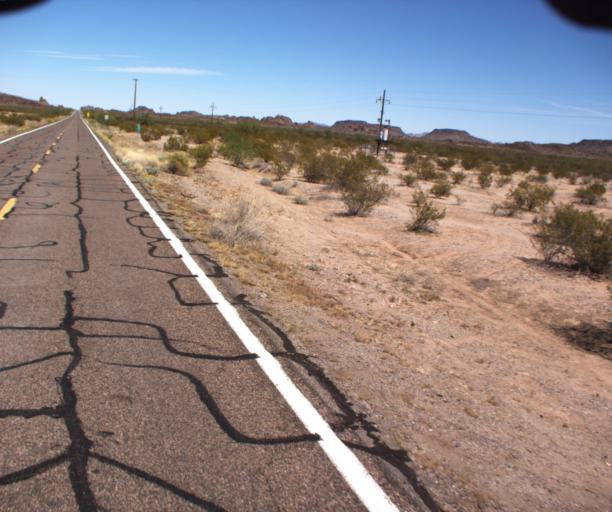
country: US
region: Arizona
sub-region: Pima County
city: Ajo
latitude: 32.5270
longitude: -112.8803
